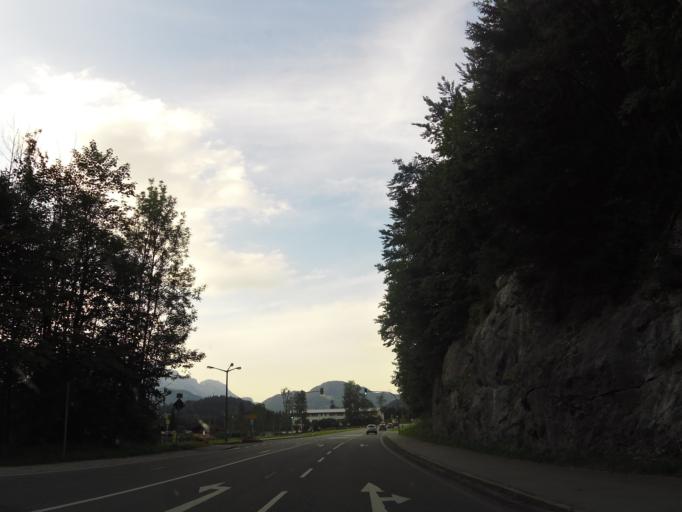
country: DE
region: Bavaria
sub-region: Upper Bavaria
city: Schoenau am Koenigssee
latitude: 47.6023
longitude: 12.9903
